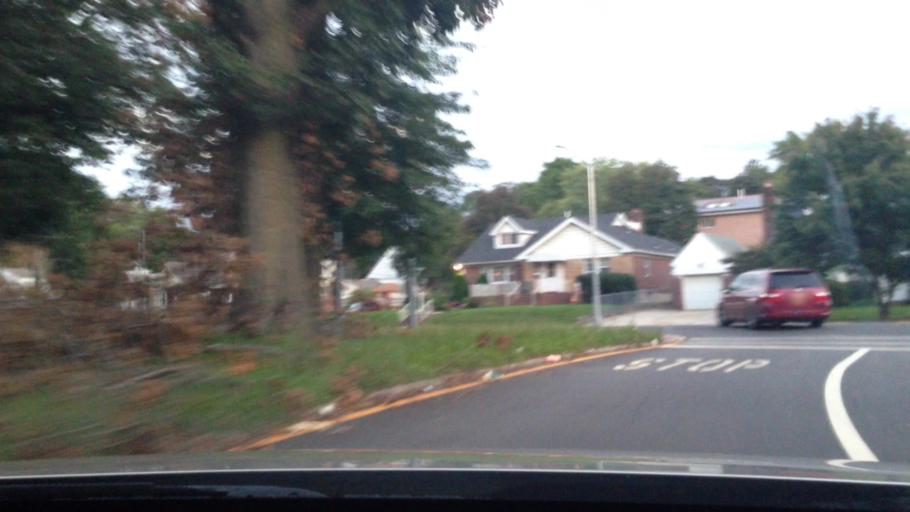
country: US
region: New York
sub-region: Nassau County
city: Bellerose Terrace
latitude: 40.7253
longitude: -73.7673
